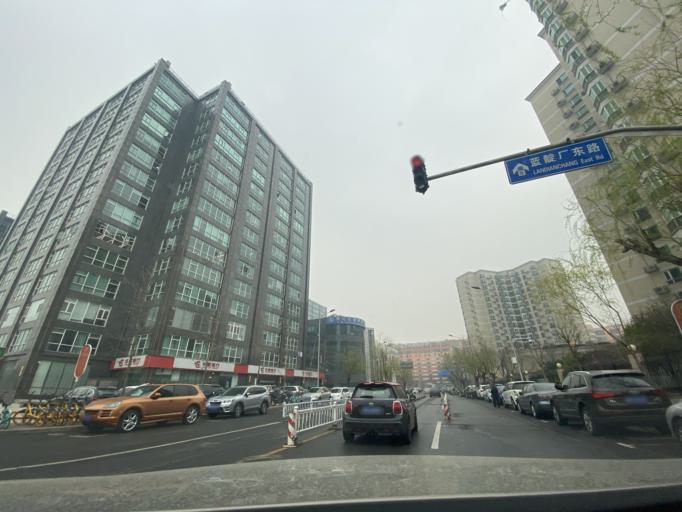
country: CN
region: Beijing
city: Sijiqing
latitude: 39.9602
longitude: 116.2813
